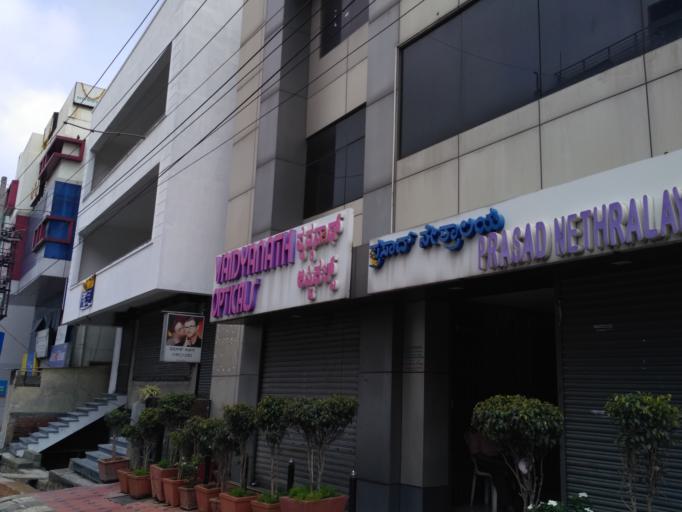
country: IN
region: Karnataka
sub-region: Bangalore Urban
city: Bangalore
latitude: 12.9604
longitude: 77.5304
